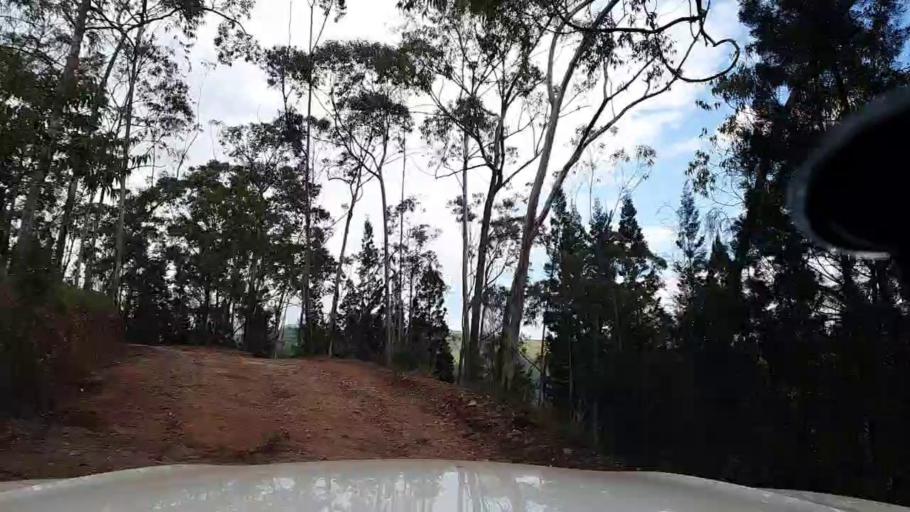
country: RW
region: Southern Province
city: Gitarama
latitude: -1.8091
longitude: 29.8031
